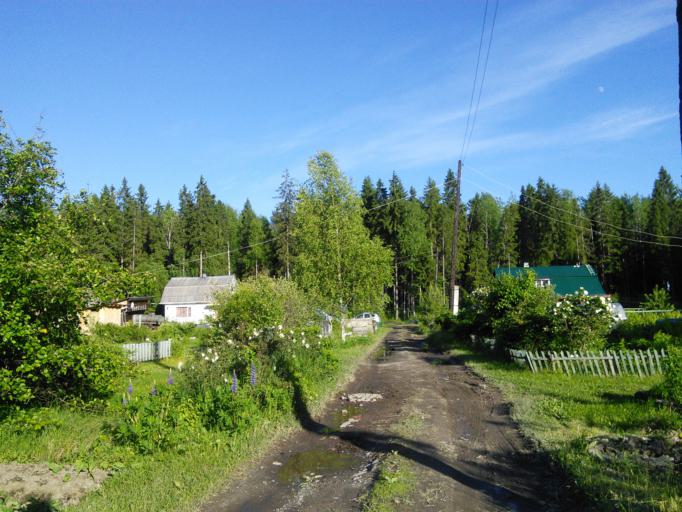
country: RU
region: Republic of Karelia
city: Shuya
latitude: 61.8492
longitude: 34.1415
